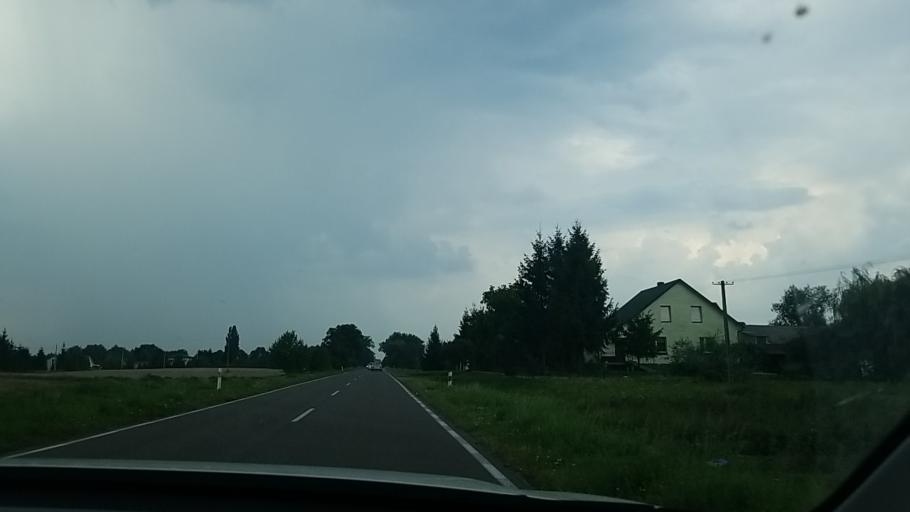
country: PL
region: Lublin Voivodeship
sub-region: Powiat leczynski
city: Cycow
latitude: 51.2608
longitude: 23.0938
